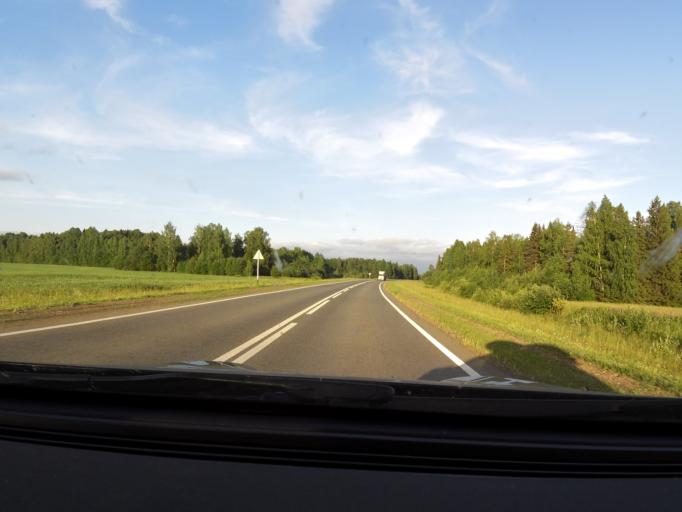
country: RU
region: Perm
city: Siva
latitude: 58.4896
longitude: 54.1203
